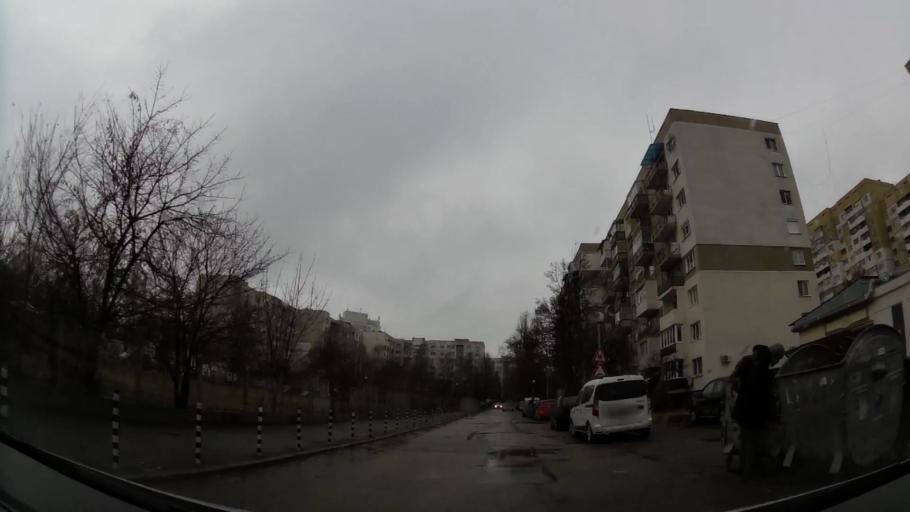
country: BG
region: Sofia-Capital
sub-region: Stolichna Obshtina
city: Sofia
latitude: 42.6434
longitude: 23.3764
